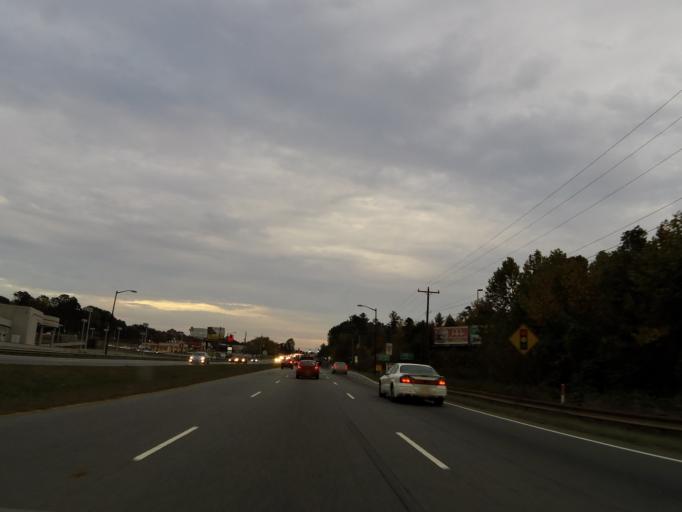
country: US
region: North Carolina
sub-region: Caldwell County
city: Northlakes
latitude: 35.7547
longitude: -81.3739
